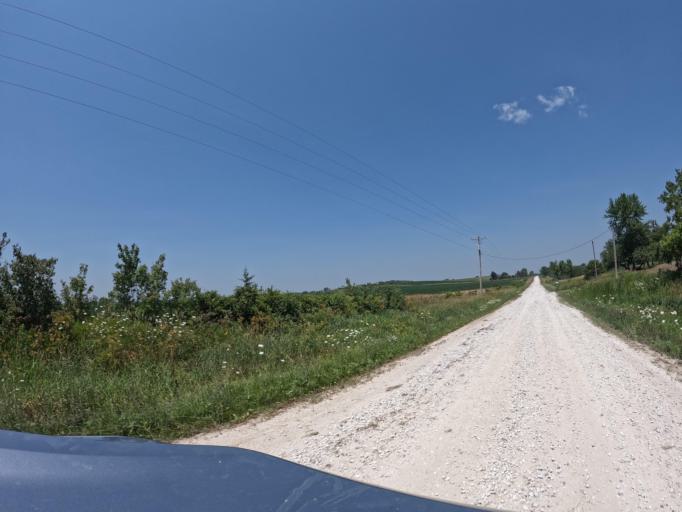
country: US
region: Iowa
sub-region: Keokuk County
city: Sigourney
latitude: 41.2901
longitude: -92.2094
